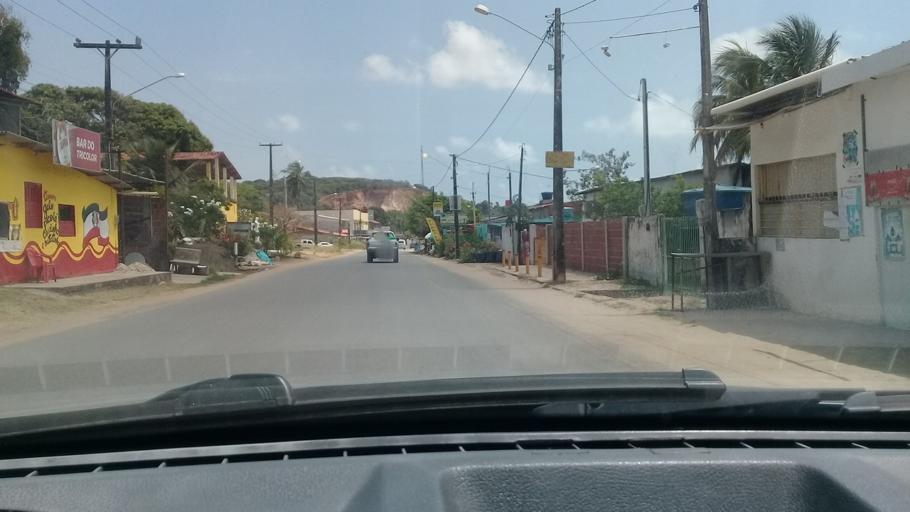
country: BR
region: Pernambuco
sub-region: Itamaraca
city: Itamaraca
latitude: -7.7887
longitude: -34.8407
